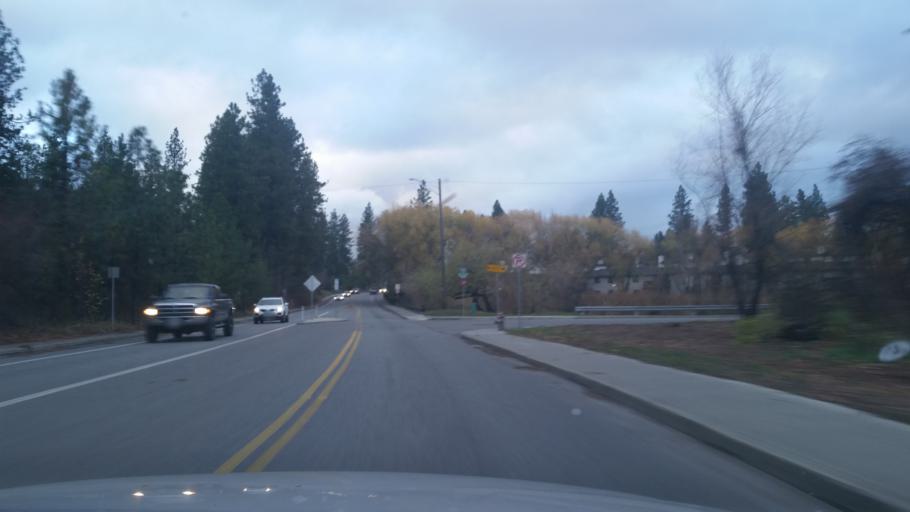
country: US
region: Washington
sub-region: Spokane County
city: Spokane
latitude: 47.6314
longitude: -117.3754
